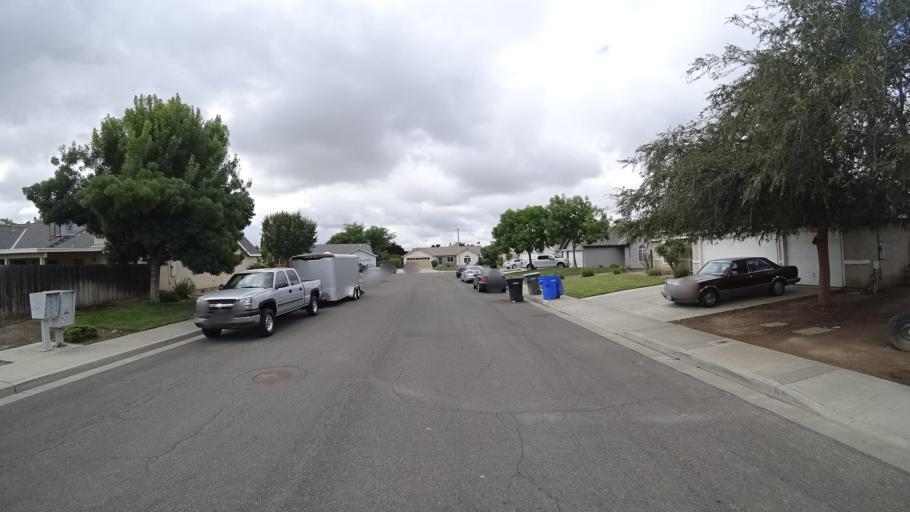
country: US
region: California
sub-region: Kings County
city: Hanford
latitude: 36.3491
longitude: -119.6630
